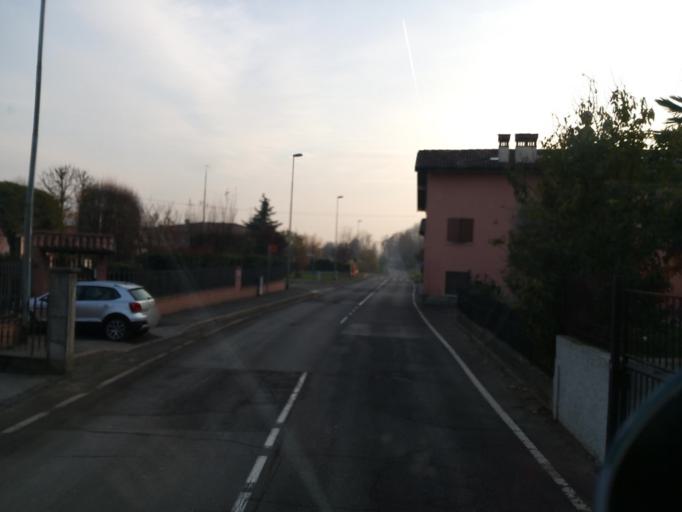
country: IT
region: Lombardy
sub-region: Provincia di Brescia
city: Poncarale
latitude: 45.4588
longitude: 10.1718
